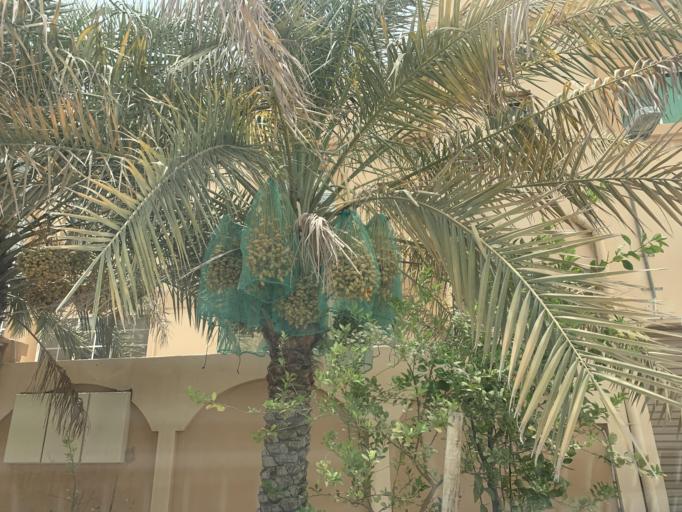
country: BH
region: Manama
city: Jidd Hafs
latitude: 26.2149
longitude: 50.5024
